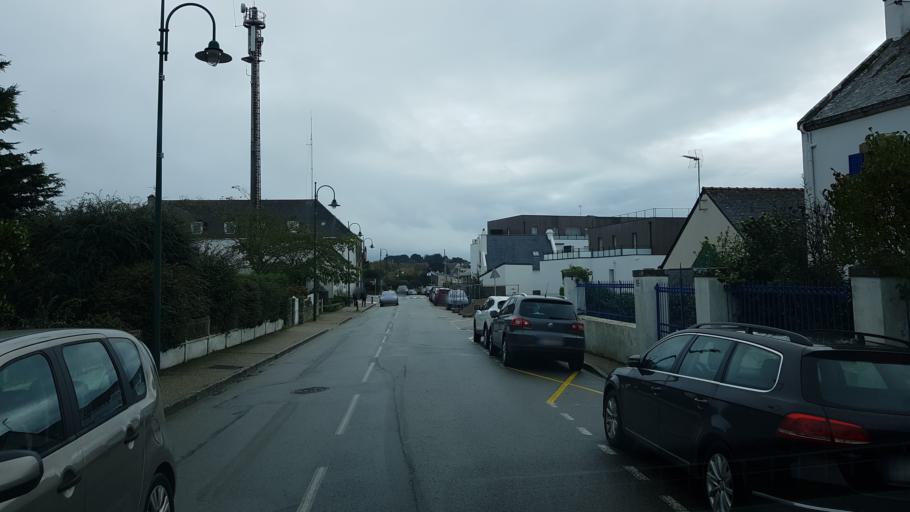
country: FR
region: Brittany
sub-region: Departement du Morbihan
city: Arzon
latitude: 47.5486
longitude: -2.8927
